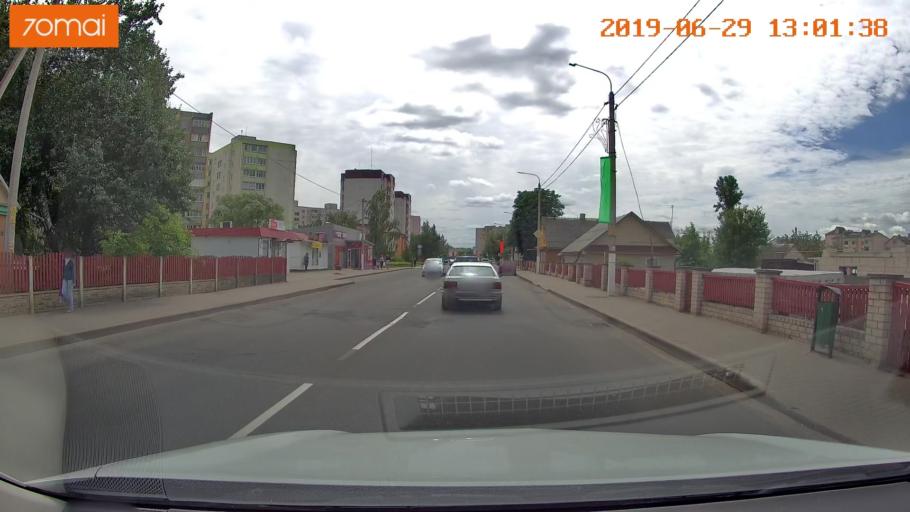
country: BY
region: Minsk
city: Slutsk
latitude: 53.0375
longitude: 27.5597
